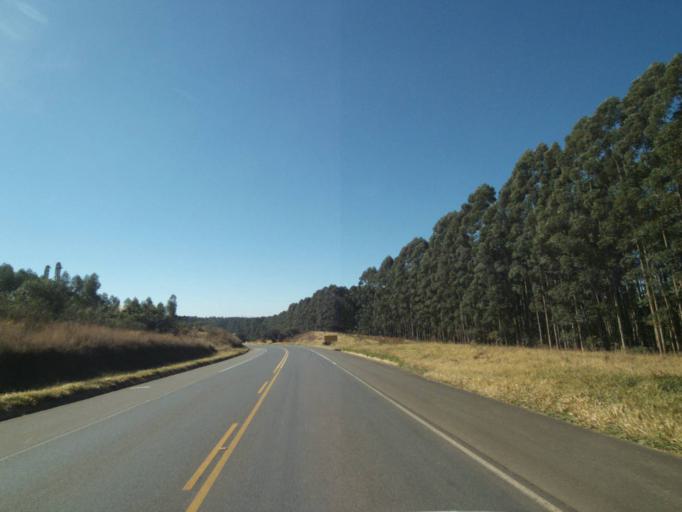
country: BR
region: Parana
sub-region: Tibagi
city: Tibagi
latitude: -24.5236
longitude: -50.4408
